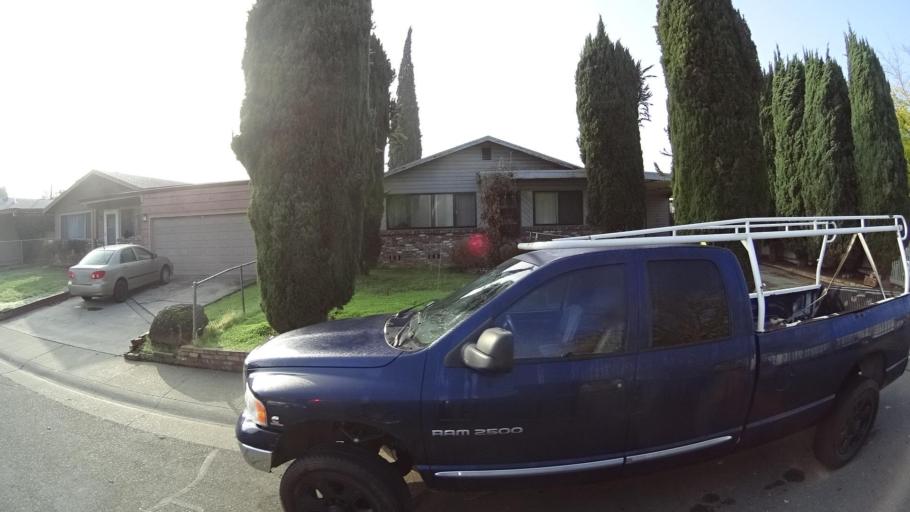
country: US
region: California
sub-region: Sacramento County
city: Elk Grove
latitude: 38.4039
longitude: -121.3545
